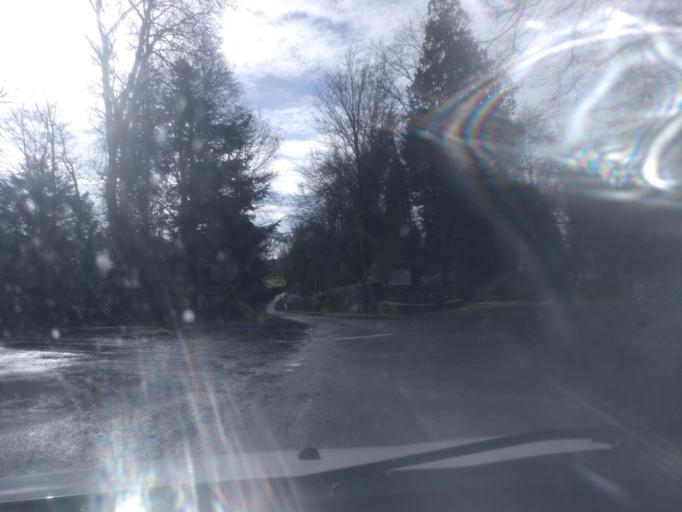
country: FR
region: Brittany
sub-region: Departement d'Ille-et-Vilaine
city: Antrain
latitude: 48.4492
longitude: -1.4865
